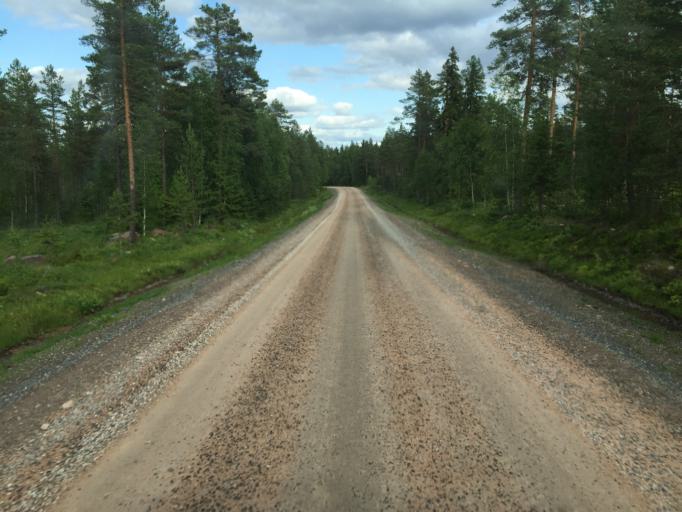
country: SE
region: Dalarna
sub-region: Malung-Saelens kommun
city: Malung
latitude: 60.9379
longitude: 13.8341
